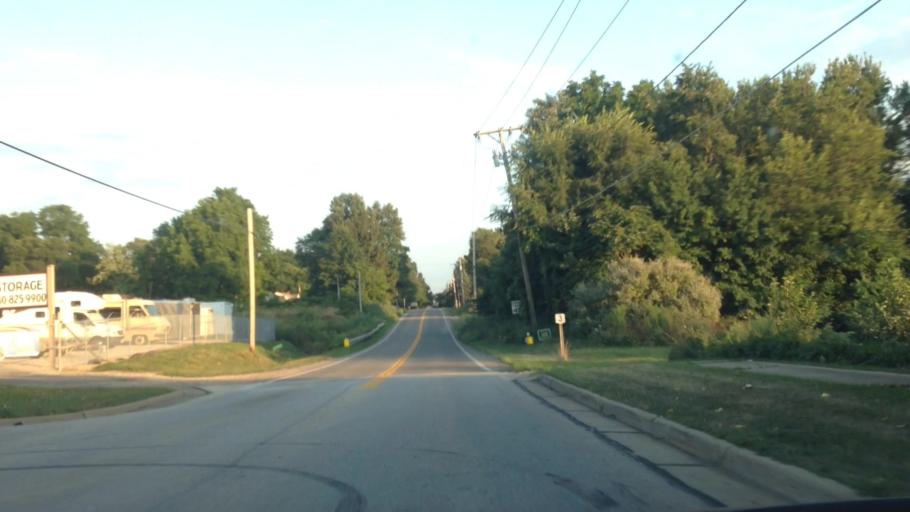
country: US
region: Ohio
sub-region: Summit County
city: Barberton
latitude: 40.9994
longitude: -81.5860
